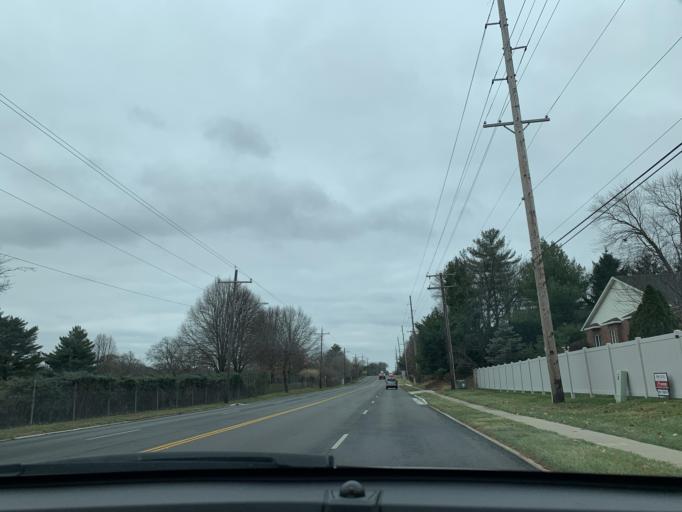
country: US
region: Illinois
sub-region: Sangamon County
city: Leland Grove
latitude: 39.7862
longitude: -89.6870
